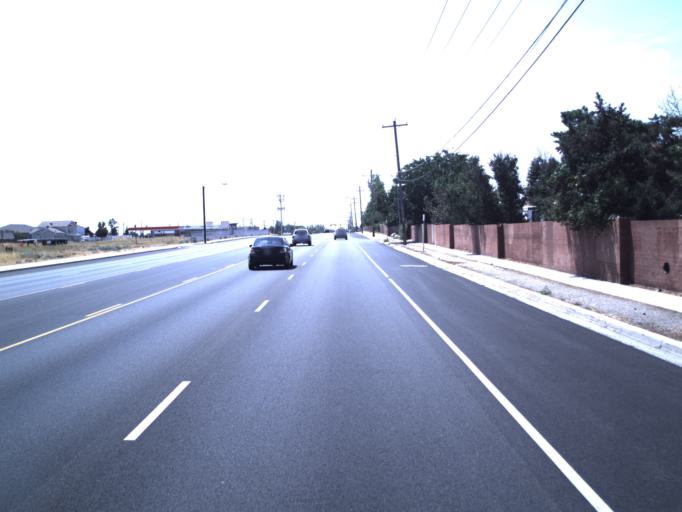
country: US
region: Utah
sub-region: Salt Lake County
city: Oquirrh
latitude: 40.6434
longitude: -112.0247
